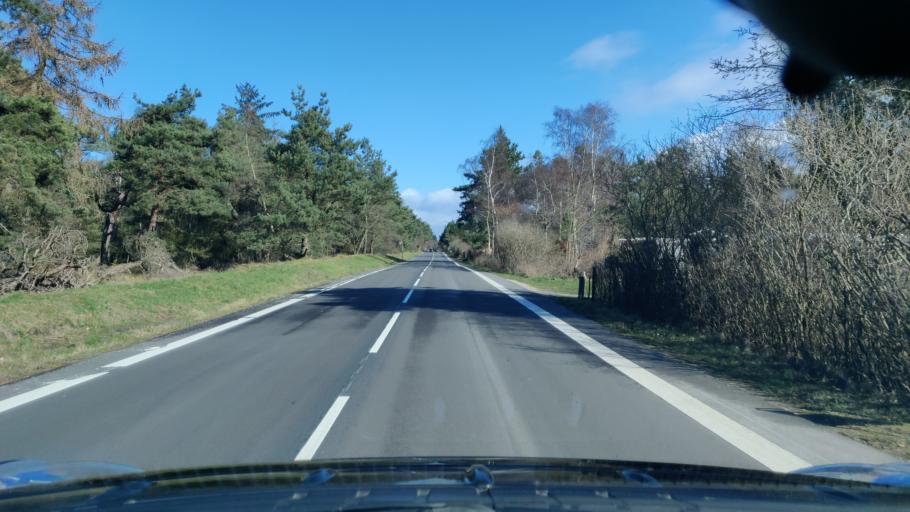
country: DK
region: Zealand
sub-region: Odsherred Kommune
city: Hojby
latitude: 55.8867
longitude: 11.5533
